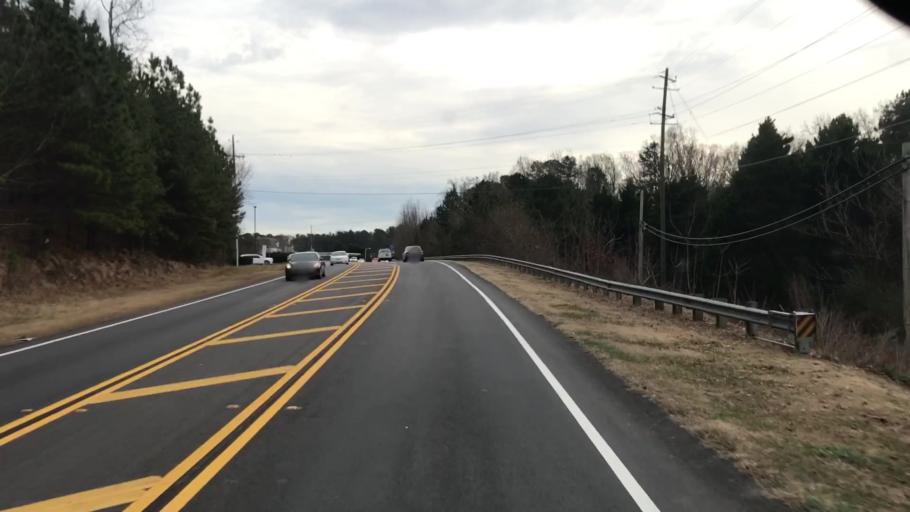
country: US
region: Georgia
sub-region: Jackson County
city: Braselton
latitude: 34.1045
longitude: -83.8151
